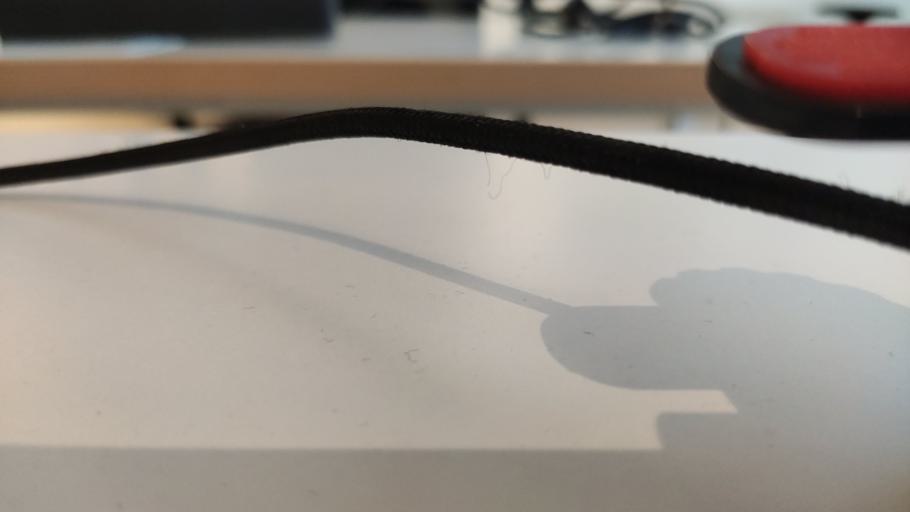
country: RU
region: Moskovskaya
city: Novopetrovskoye
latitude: 55.9335
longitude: 36.4343
